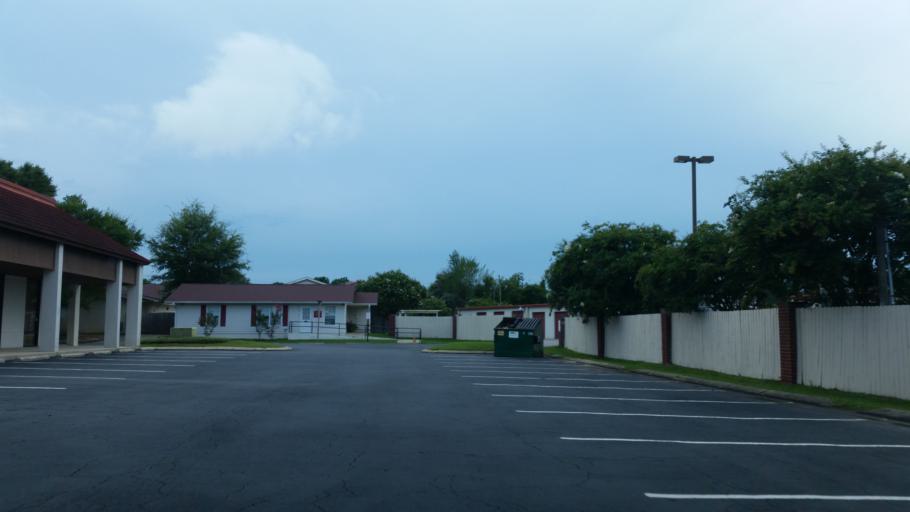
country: US
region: Florida
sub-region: Escambia County
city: Ferry Pass
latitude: 30.5012
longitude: -87.1850
